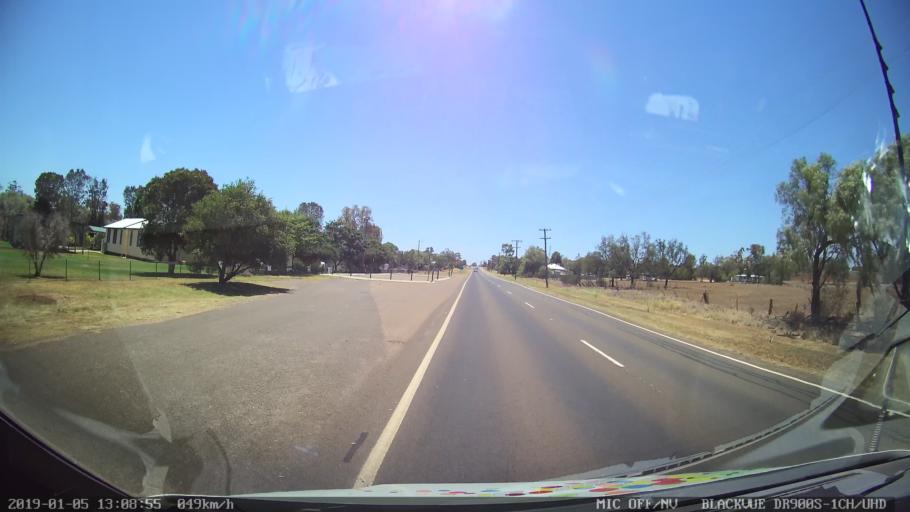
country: AU
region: New South Wales
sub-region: Gunnedah
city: Gunnedah
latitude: -31.0995
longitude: 149.9062
